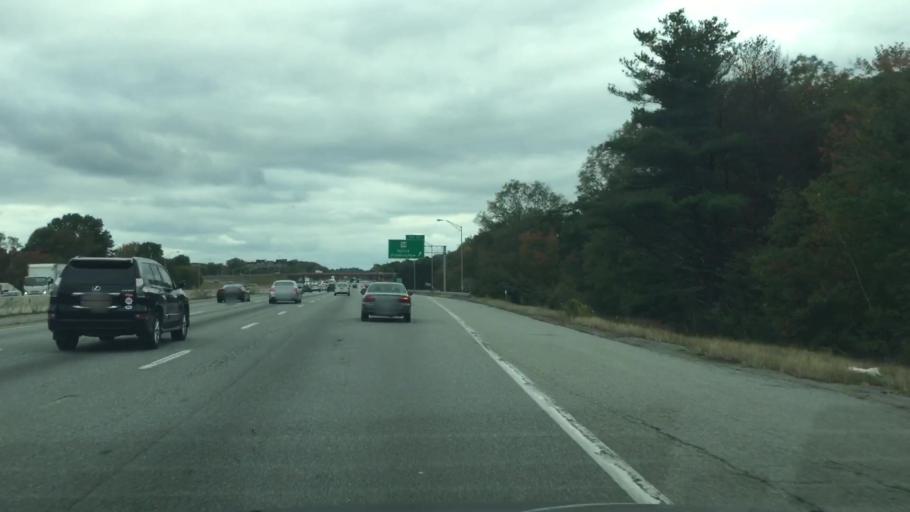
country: US
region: Massachusetts
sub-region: Middlesex County
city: Cochituate
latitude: 42.3118
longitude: -71.3770
